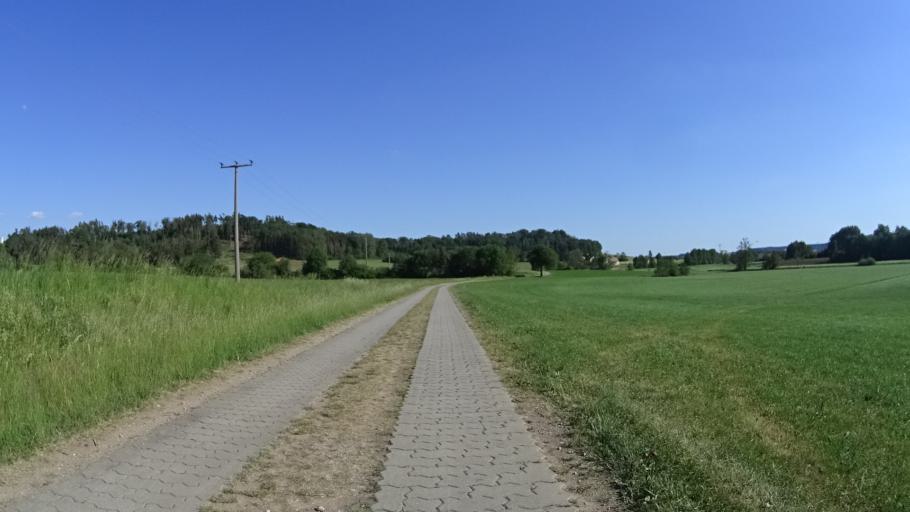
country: DE
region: Bavaria
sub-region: Regierungsbezirk Mittelfranken
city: Feuchtwangen
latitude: 49.1893
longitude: 10.3239
